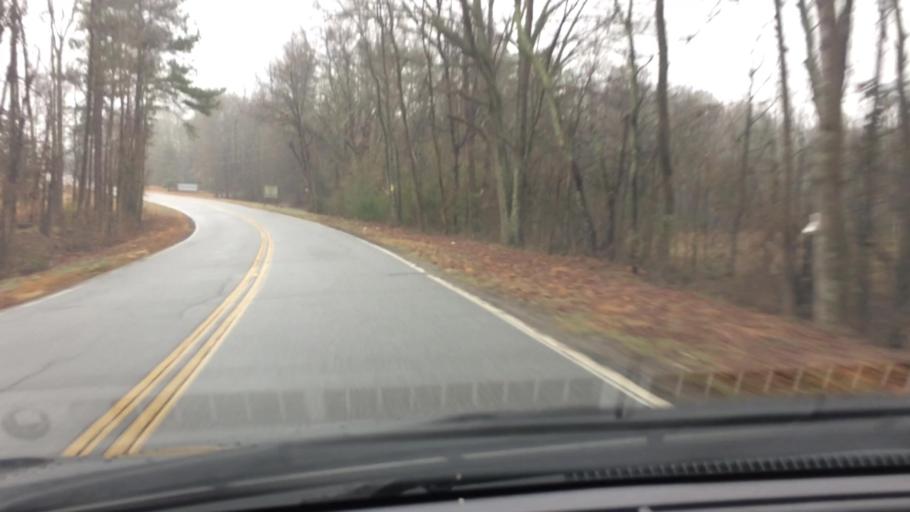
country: US
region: South Carolina
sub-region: Anderson County
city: Williamston
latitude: 34.6345
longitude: -82.4811
